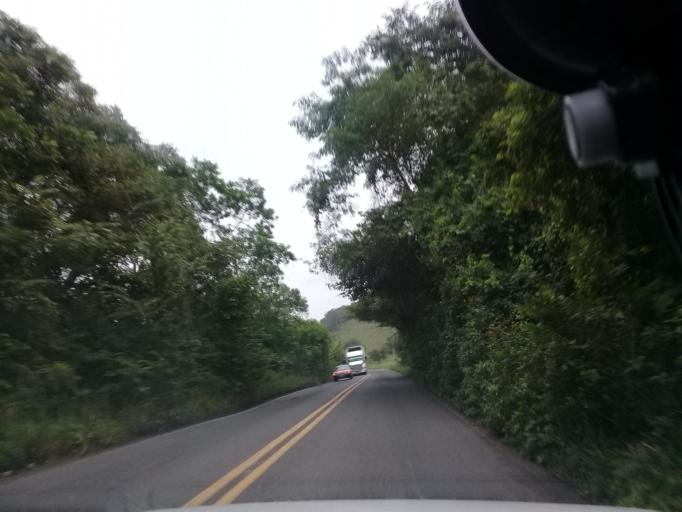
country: MX
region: Veracruz
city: Platon Sanchez
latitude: 21.2415
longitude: -98.3659
